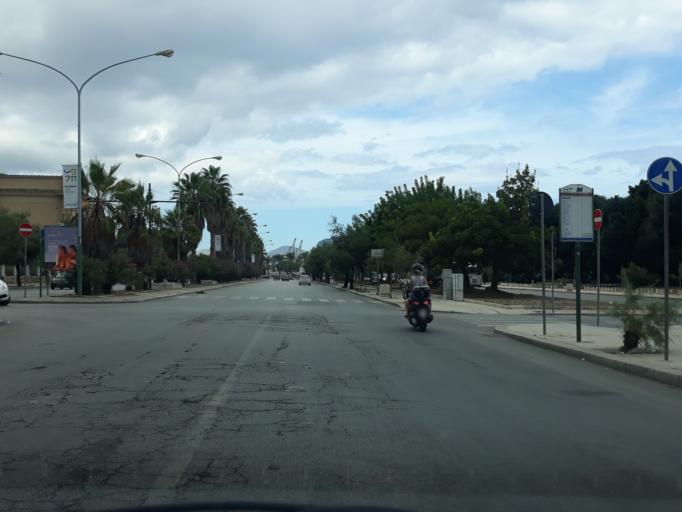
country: IT
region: Sicily
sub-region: Palermo
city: Palermo
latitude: 38.1133
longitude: 13.3778
